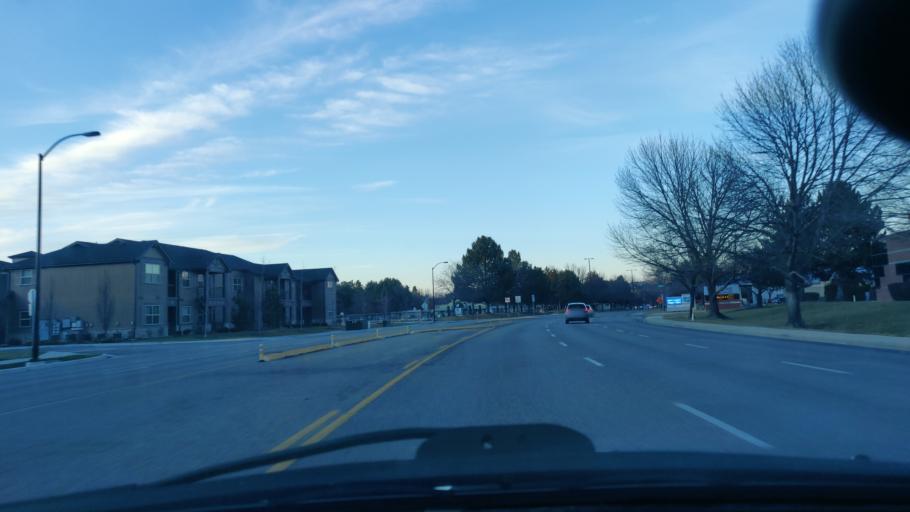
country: US
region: Idaho
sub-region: Ada County
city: Boise
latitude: 43.5925
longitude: -116.1777
